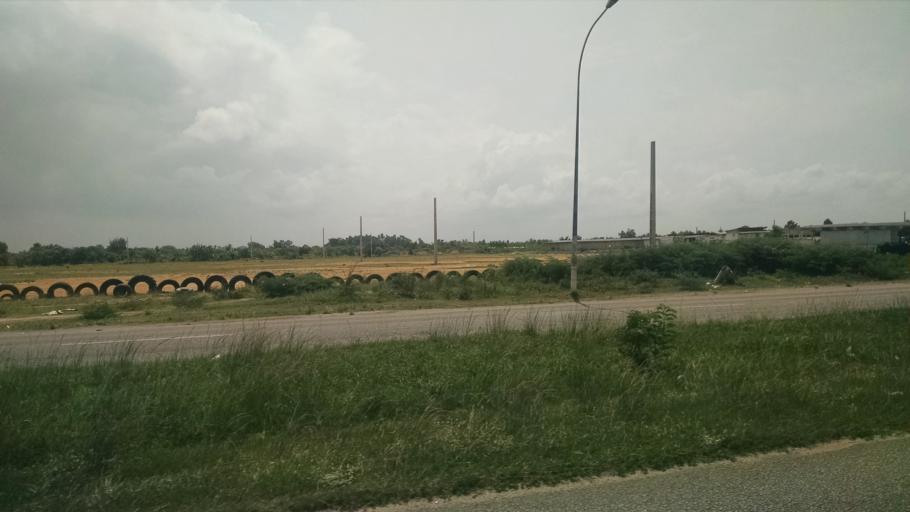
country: CI
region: Lagunes
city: Abidjan
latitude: 5.2630
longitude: -3.9493
